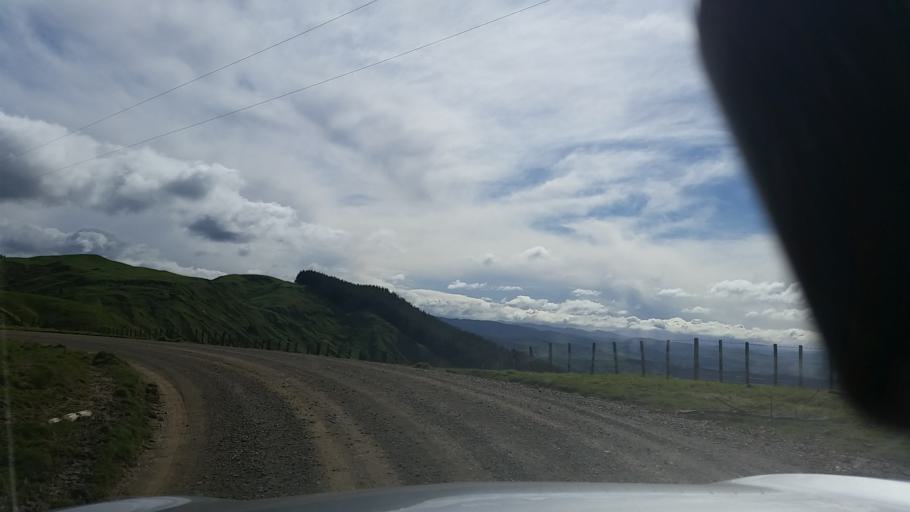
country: NZ
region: Hawke's Bay
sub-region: Napier City
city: Napier
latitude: -39.2099
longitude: 176.9641
